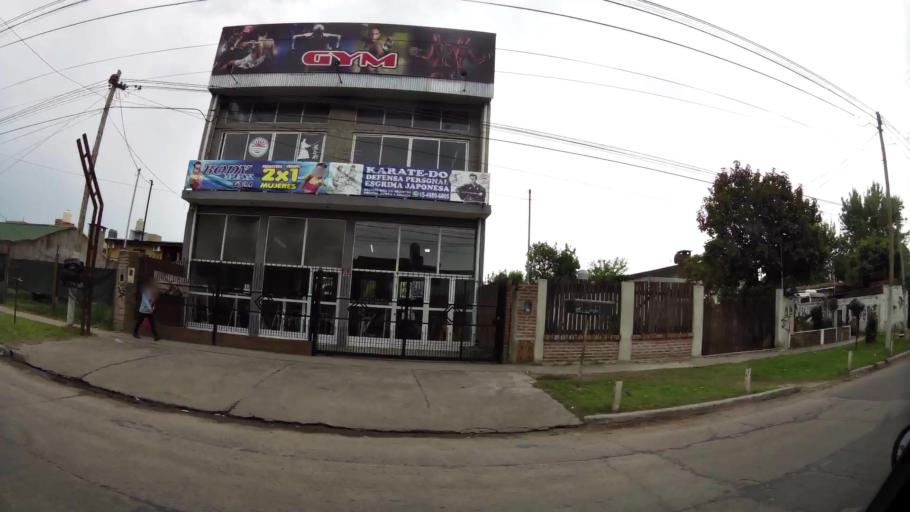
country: AR
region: Buenos Aires
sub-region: Partido de Quilmes
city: Quilmes
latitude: -34.7913
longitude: -58.2474
